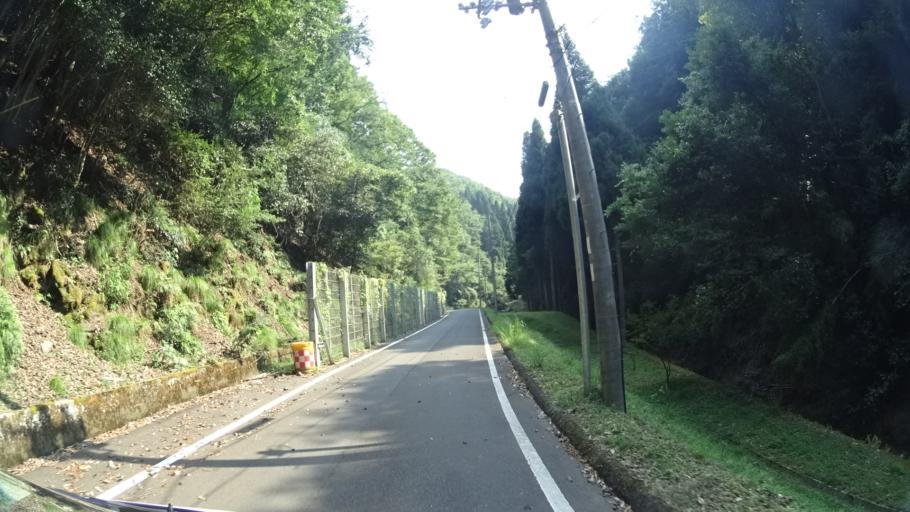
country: JP
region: Kyoto
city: Maizuru
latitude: 35.4047
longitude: 135.2409
